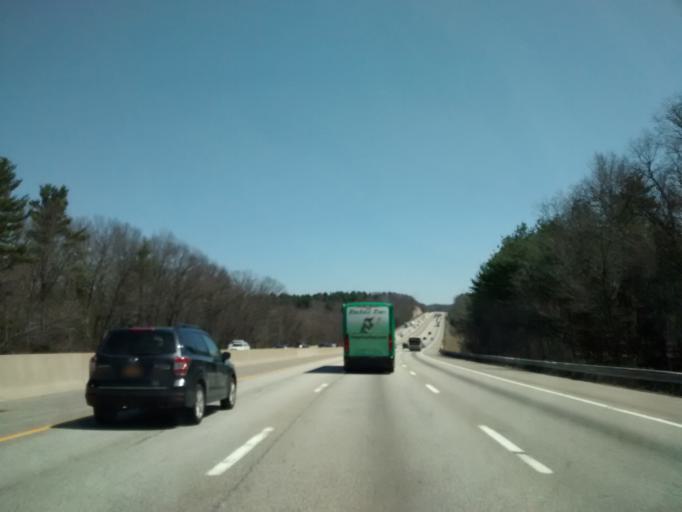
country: US
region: Massachusetts
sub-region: Worcester County
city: Grafton
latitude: 42.2287
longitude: -71.6553
